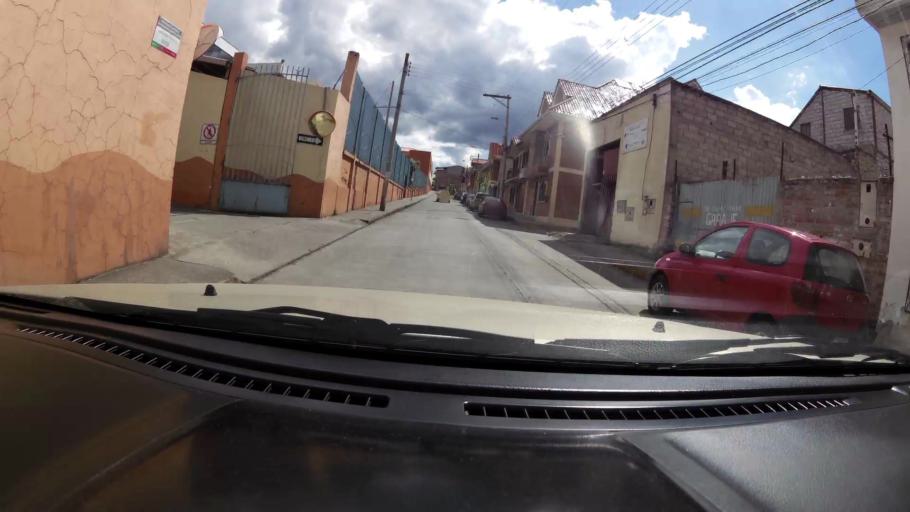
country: EC
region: Azuay
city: Cuenca
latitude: -2.8855
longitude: -78.9907
